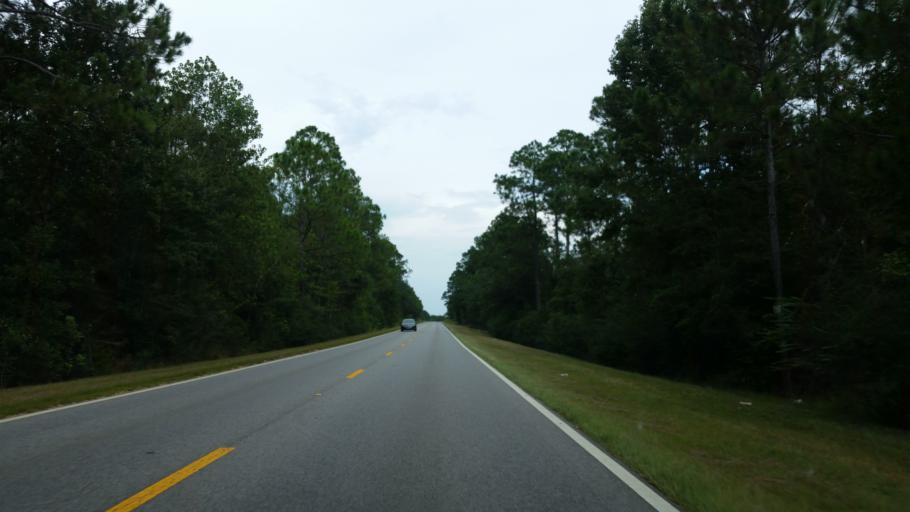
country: US
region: Florida
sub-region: Santa Rosa County
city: Wallace
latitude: 30.6727
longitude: -87.2305
